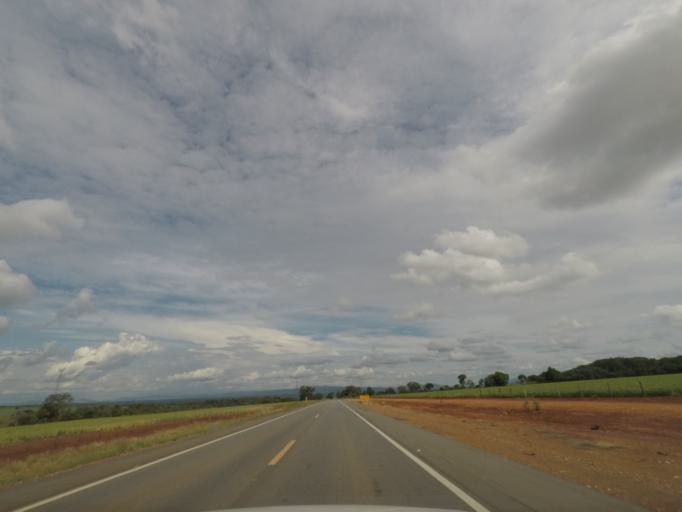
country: BR
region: Goias
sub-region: Uruacu
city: Uruacu
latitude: -14.6992
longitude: -49.1094
